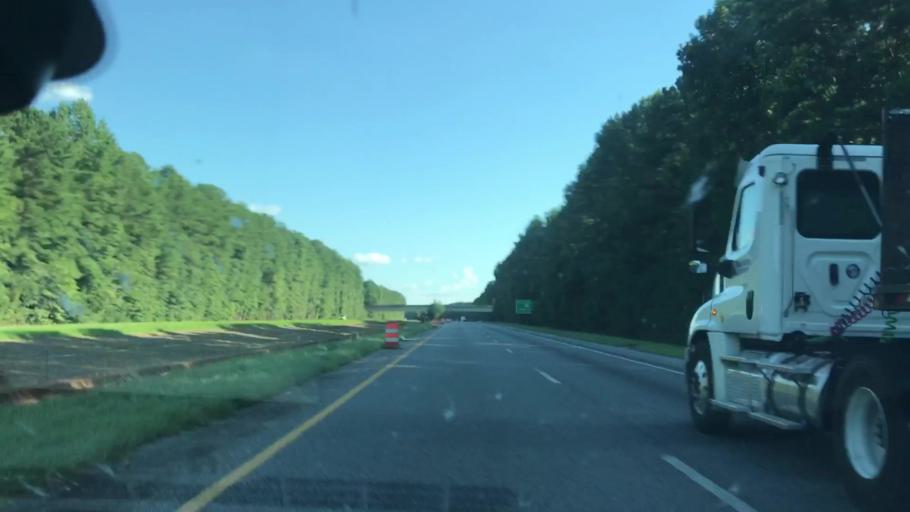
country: US
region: Georgia
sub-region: Harris County
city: Hamilton
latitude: 32.6829
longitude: -84.9903
